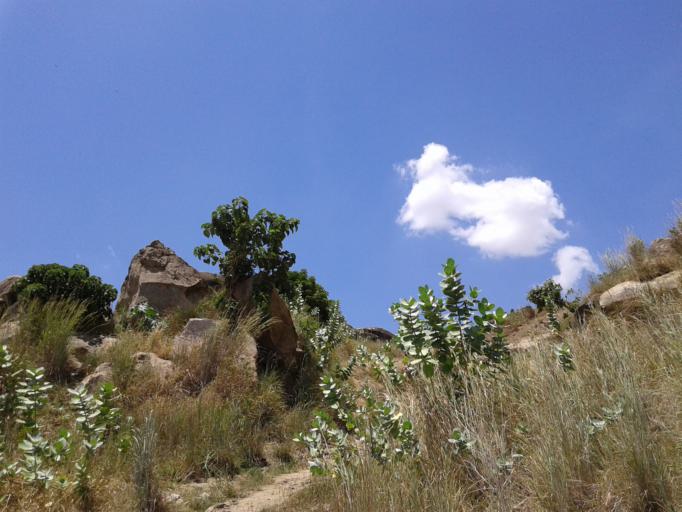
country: SS
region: Central Equatoria
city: Juba
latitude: 4.8463
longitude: 31.5515
